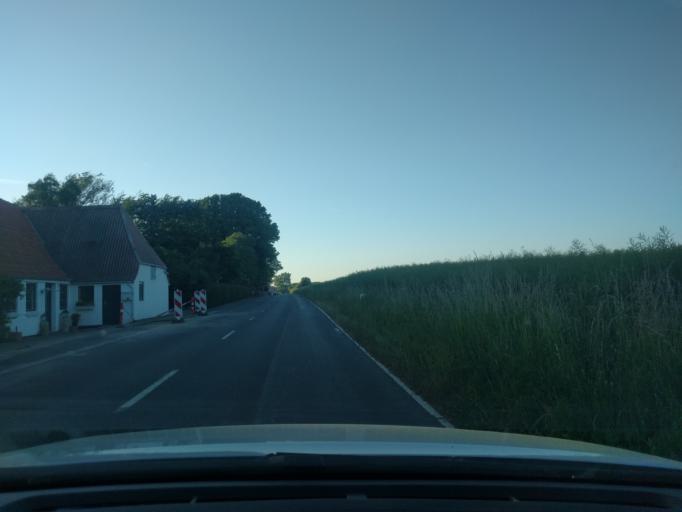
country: DK
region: South Denmark
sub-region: Kerteminde Kommune
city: Kerteminde
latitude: 55.5990
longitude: 10.6253
